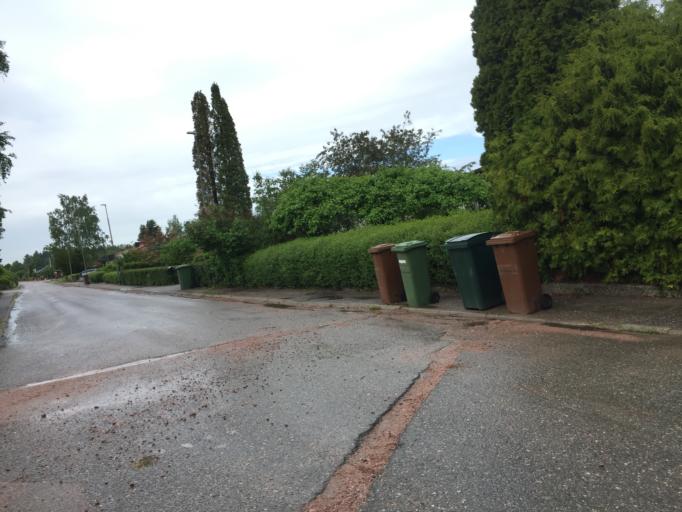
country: SE
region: Vaestmanland
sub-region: Hallstahammars Kommun
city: Hallstahammar
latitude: 59.6237
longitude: 16.2466
